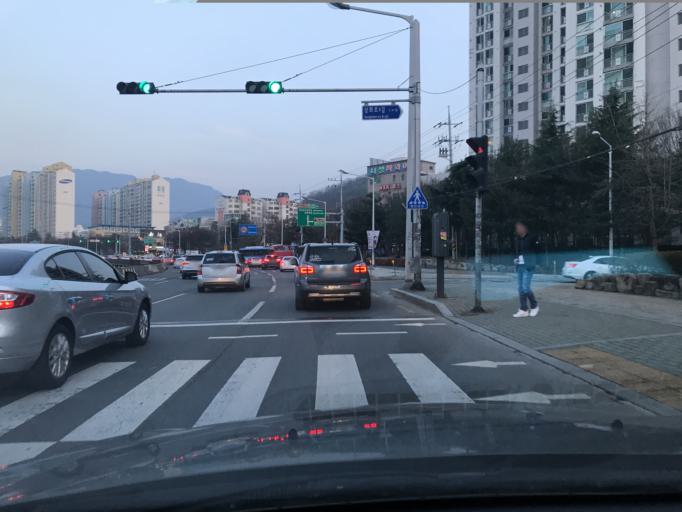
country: KR
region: Daegu
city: Hwawon
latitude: 35.8083
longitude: 128.5182
